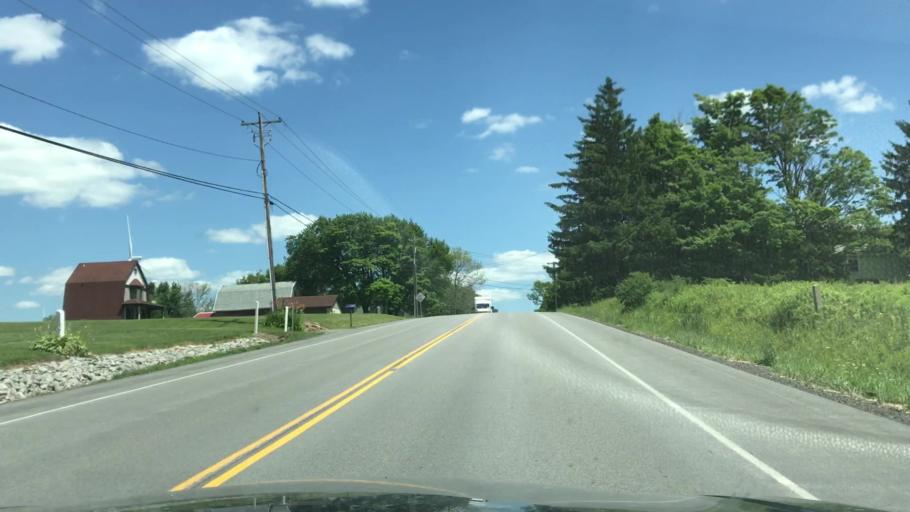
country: US
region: New York
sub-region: Erie County
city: Alden
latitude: 42.7698
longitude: -78.4319
